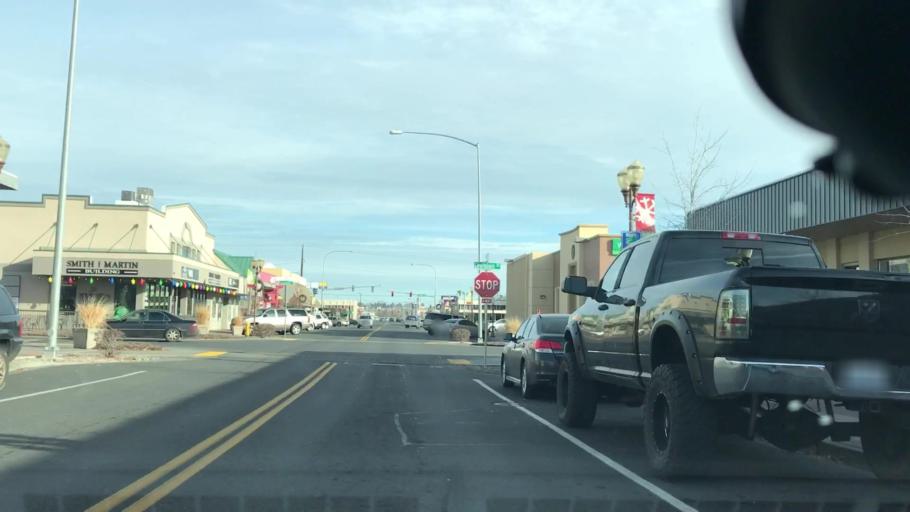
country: US
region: Washington
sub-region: Grant County
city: Moses Lake
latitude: 47.1300
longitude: -119.2784
